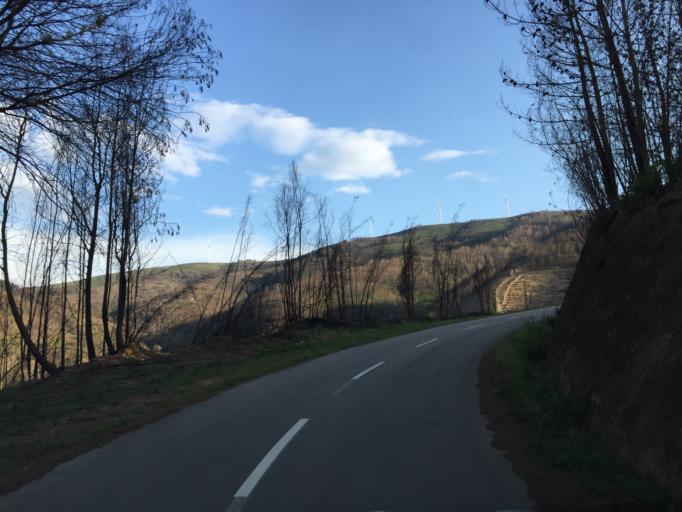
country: PT
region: Coimbra
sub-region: Pampilhosa da Serra
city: Pampilhosa da Serra
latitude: 40.1342
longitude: -7.9926
